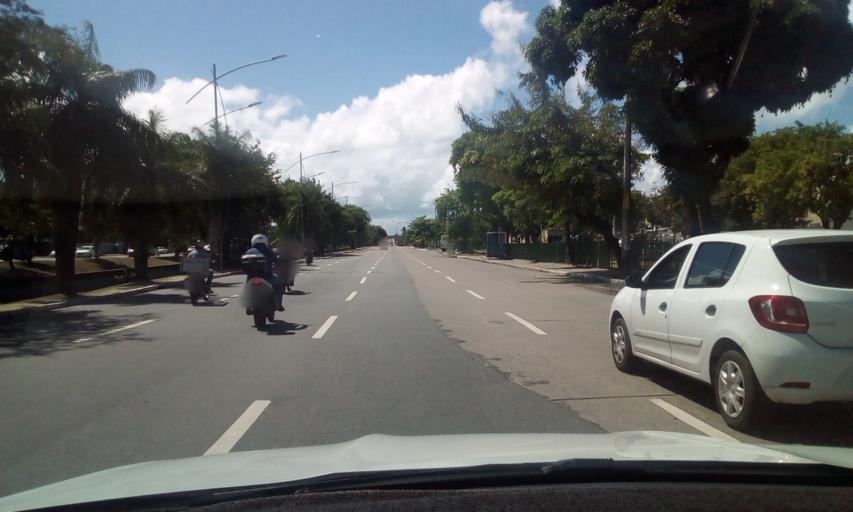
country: BR
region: Pernambuco
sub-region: Recife
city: Recife
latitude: -8.0397
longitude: -34.8783
